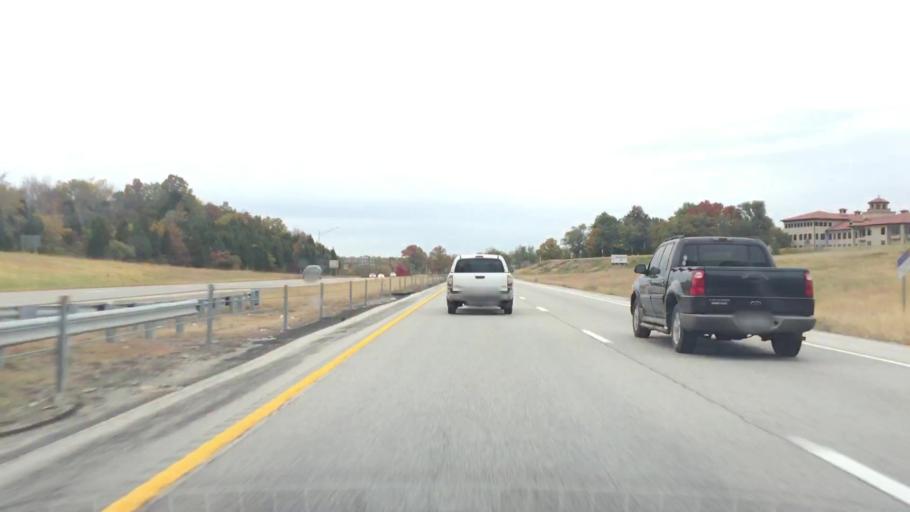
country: US
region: Missouri
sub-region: Jackson County
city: Lees Summit
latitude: 38.9445
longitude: -94.4090
